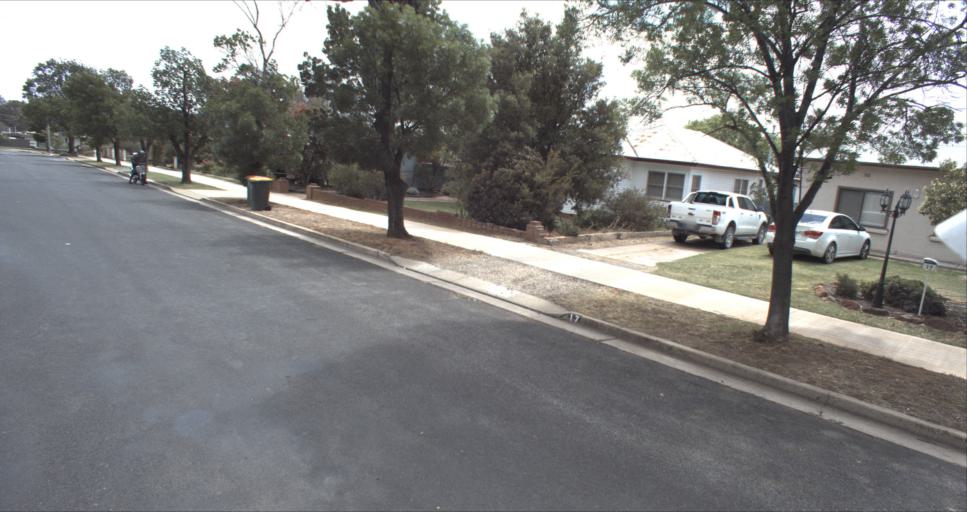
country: AU
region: New South Wales
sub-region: Leeton
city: Leeton
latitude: -34.5610
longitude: 146.3946
